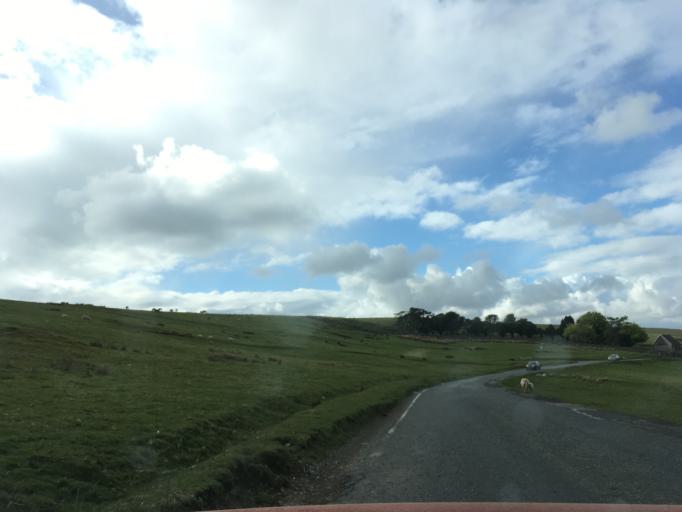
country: GB
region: Wales
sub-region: Caerphilly County Borough
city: Rhymney
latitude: 51.7292
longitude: -3.2989
